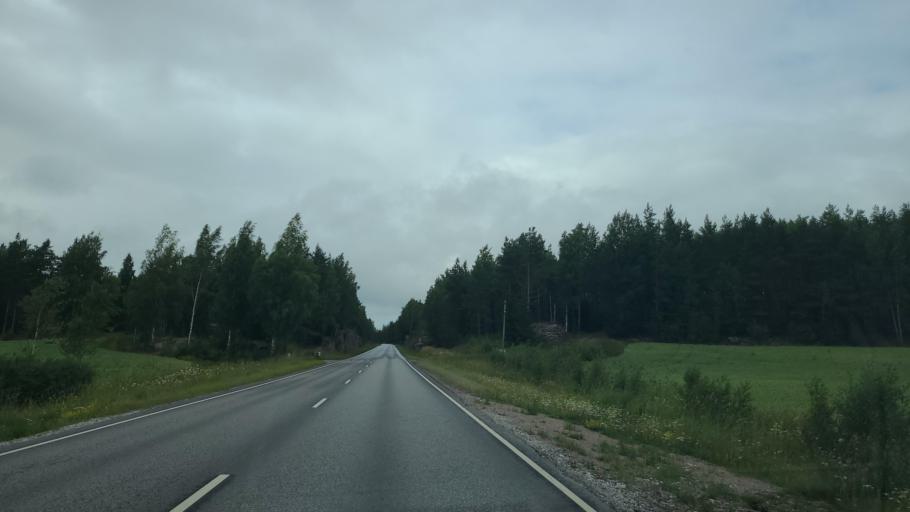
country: FI
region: Varsinais-Suomi
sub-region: Aboland-Turunmaa
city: Kimito
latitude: 60.2162
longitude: 22.6361
